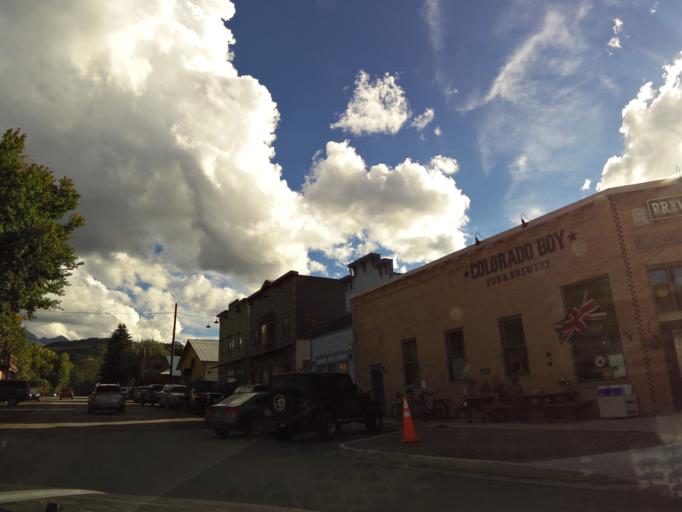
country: US
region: Colorado
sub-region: Ouray County
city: Ouray
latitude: 38.1524
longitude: -107.7576
